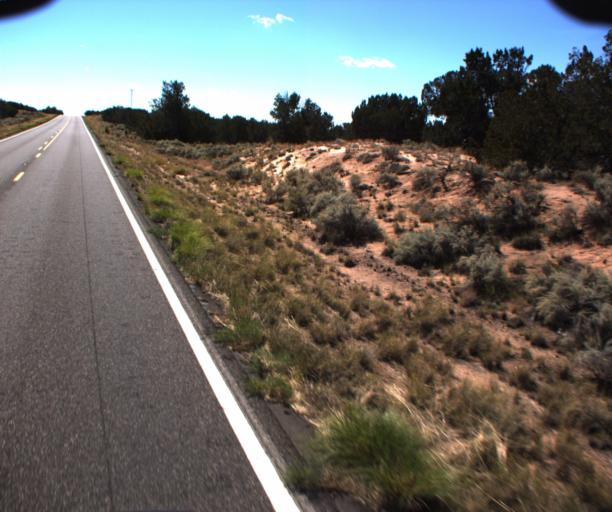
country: US
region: Arizona
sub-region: Apache County
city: Saint Johns
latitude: 34.8525
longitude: -109.2377
